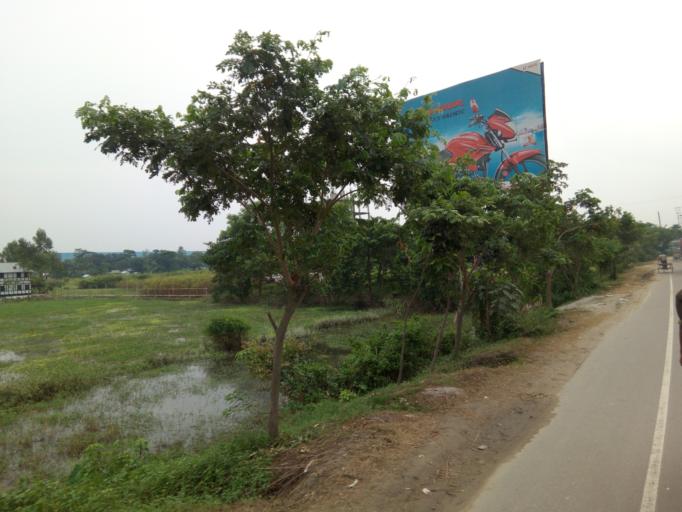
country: BD
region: Dhaka
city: Char Bhadrasan
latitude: 23.4747
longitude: 90.2844
